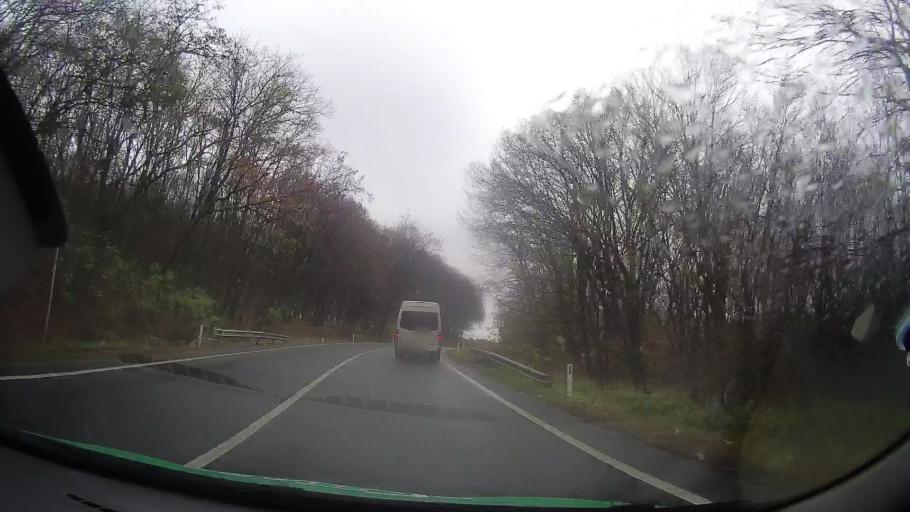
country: RO
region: Bistrita-Nasaud
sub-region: Comuna Galatii Bistritei
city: Galatii Bistritei
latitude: 47.0365
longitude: 24.4214
